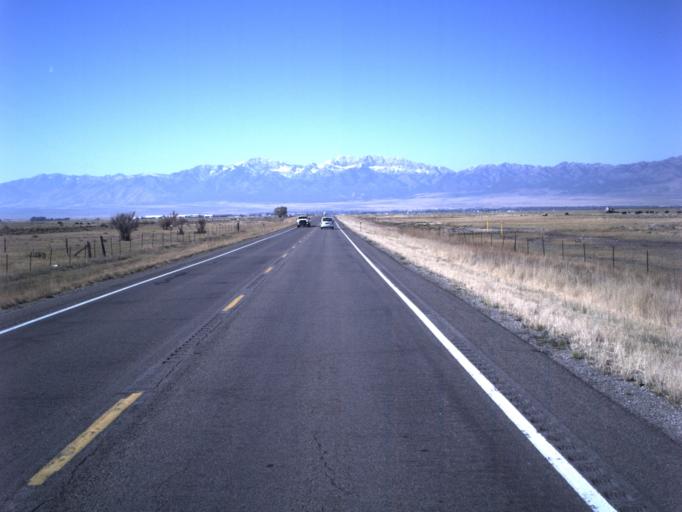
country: US
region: Utah
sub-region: Tooele County
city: Erda
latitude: 40.6294
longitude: -112.3417
